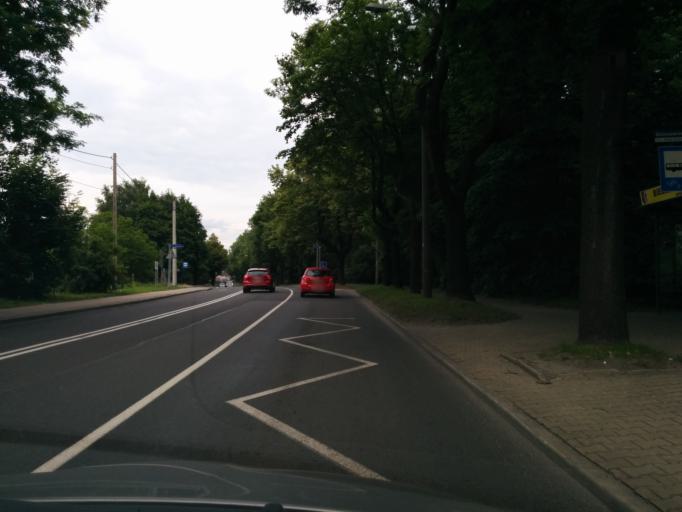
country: PL
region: Silesian Voivodeship
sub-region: Ruda Slaska
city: Ruda Slaska
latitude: 50.2715
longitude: 18.8448
